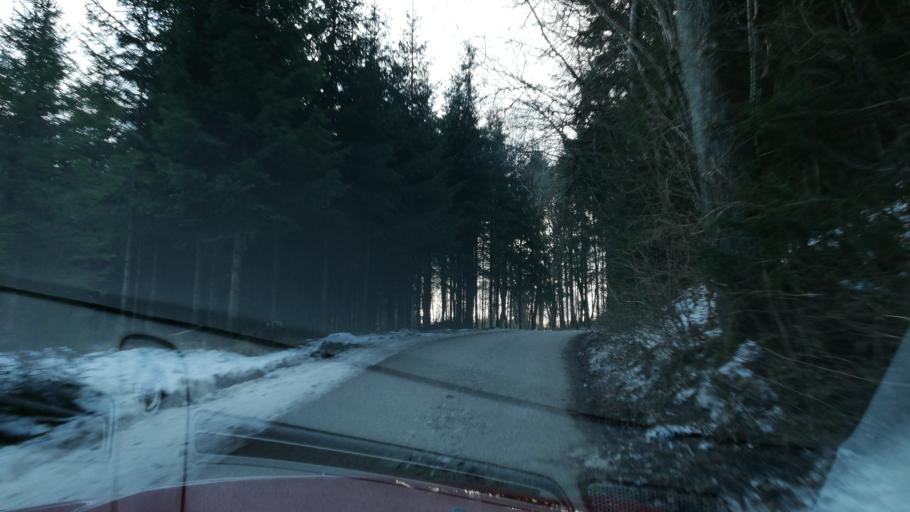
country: AT
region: Upper Austria
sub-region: Wels-Land
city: Buchkirchen
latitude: 48.2362
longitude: 13.9907
